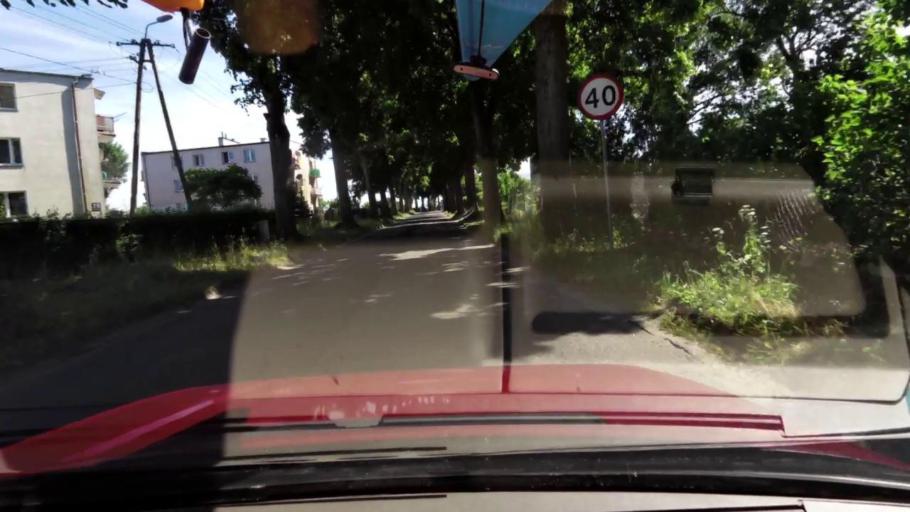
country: PL
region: Pomeranian Voivodeship
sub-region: Powiat slupski
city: Kobylnica
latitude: 54.3807
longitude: 16.9653
